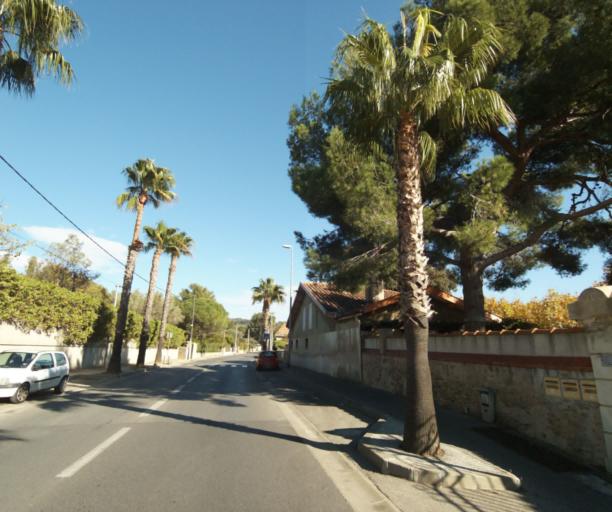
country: FR
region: Provence-Alpes-Cote d'Azur
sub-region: Departement des Bouches-du-Rhone
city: Ceyreste
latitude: 43.1897
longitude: 5.6357
